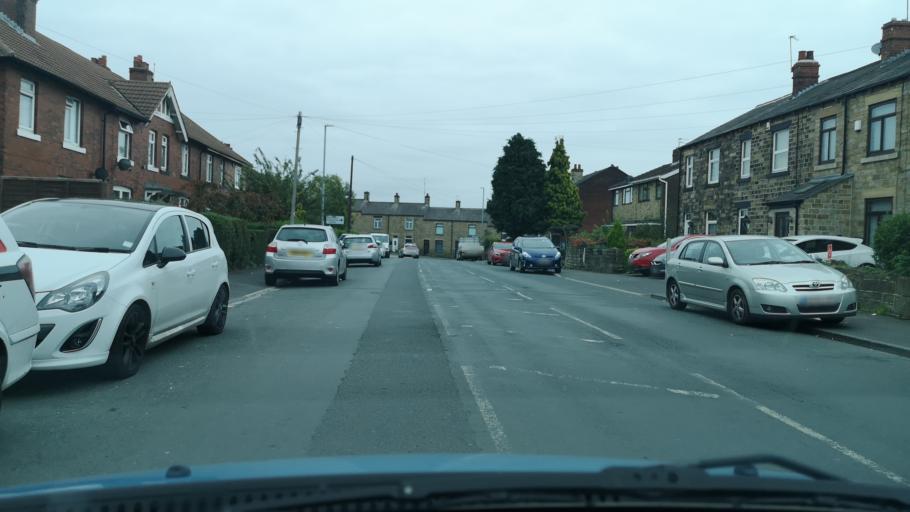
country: GB
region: England
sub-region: Kirklees
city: Dewsbury
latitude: 53.6830
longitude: -1.6513
